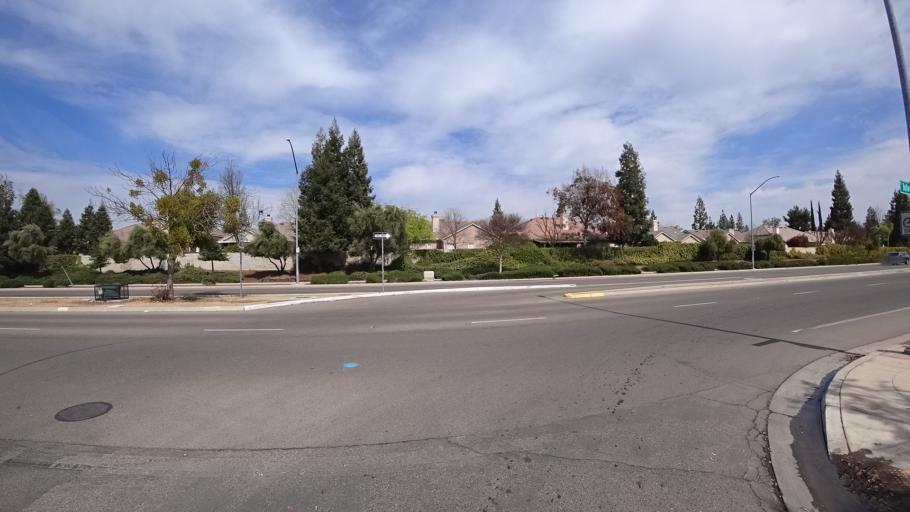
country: US
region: California
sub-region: Fresno County
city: West Park
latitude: 36.8220
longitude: -119.8765
